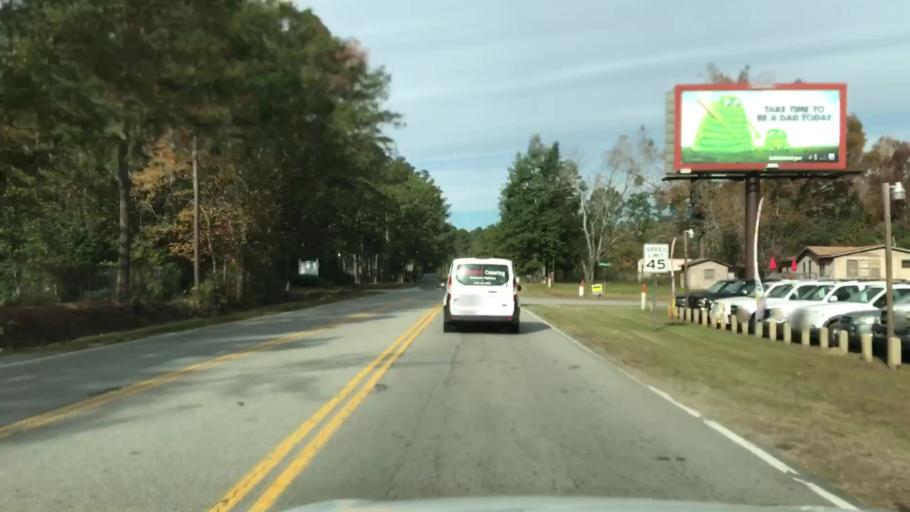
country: US
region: South Carolina
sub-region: Colleton County
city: Walterboro
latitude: 32.8916
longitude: -80.6288
